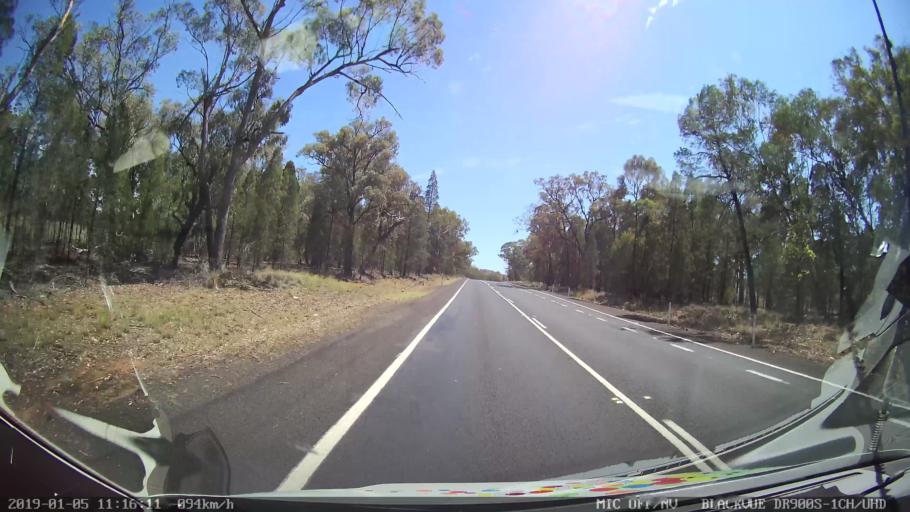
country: AU
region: New South Wales
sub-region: Warrumbungle Shire
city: Coonabarabran
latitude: -31.3423
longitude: 149.2970
